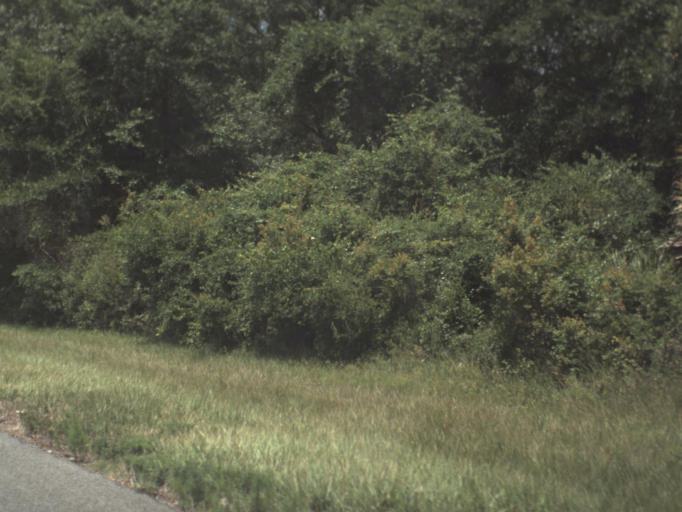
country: US
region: Florida
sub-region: Taylor County
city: Perry
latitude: 30.0898
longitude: -83.6471
